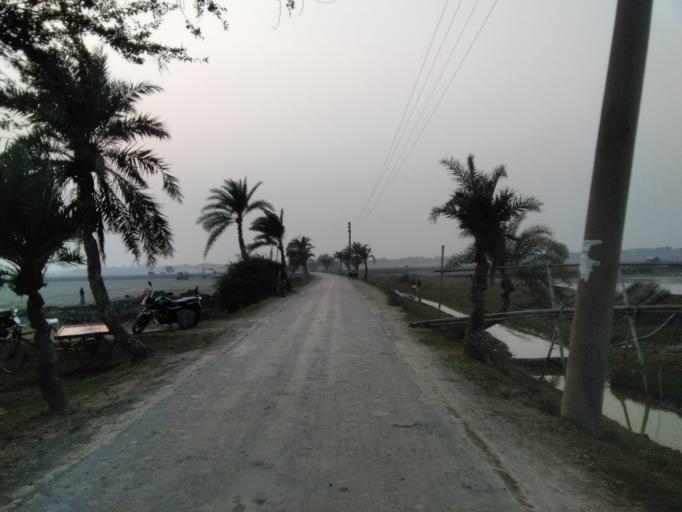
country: BD
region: Khulna
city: Satkhira
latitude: 22.6494
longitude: 89.0096
